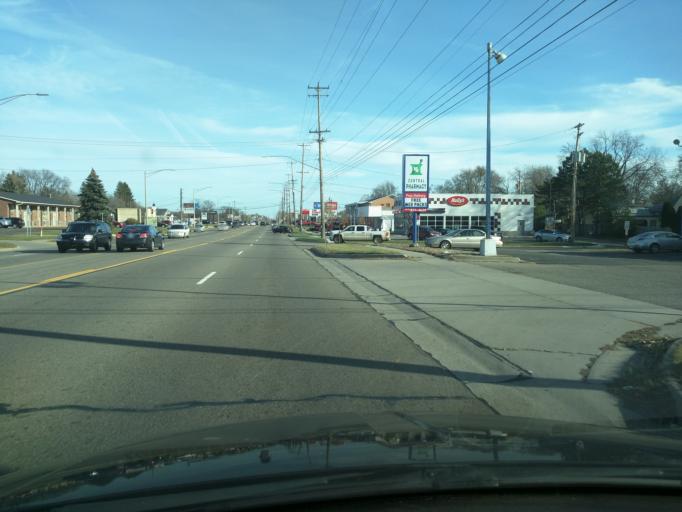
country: US
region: Michigan
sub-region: Eaton County
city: Waverly
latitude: 42.7410
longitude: -84.6177
